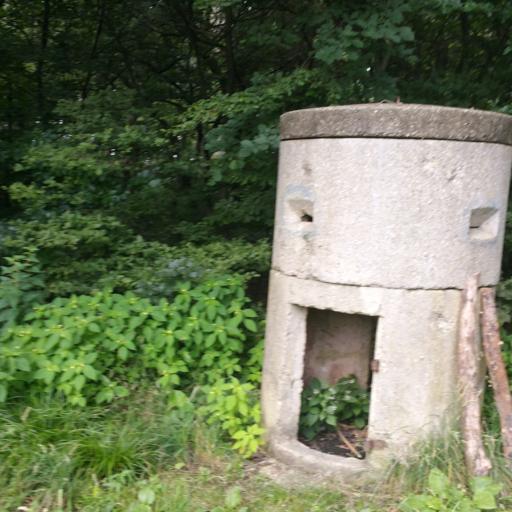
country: AT
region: Lower Austria
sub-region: Politischer Bezirk Wien-Umgebung
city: Purkersdorf
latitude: 48.2219
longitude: 16.2671
